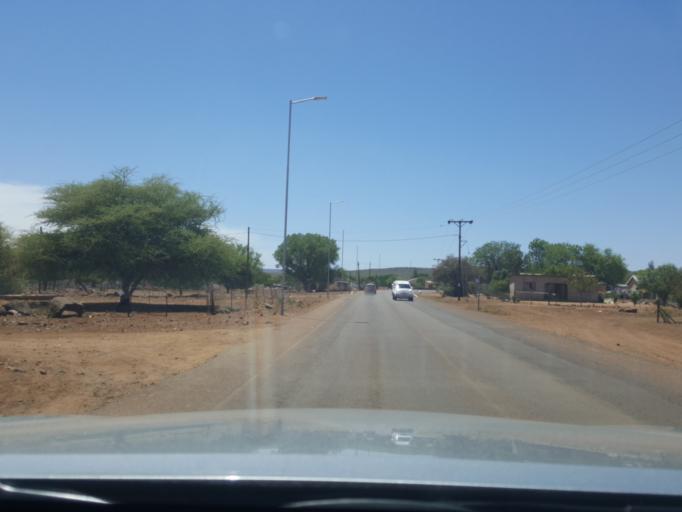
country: BW
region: South East
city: Ramotswa
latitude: -24.8693
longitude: 25.8779
